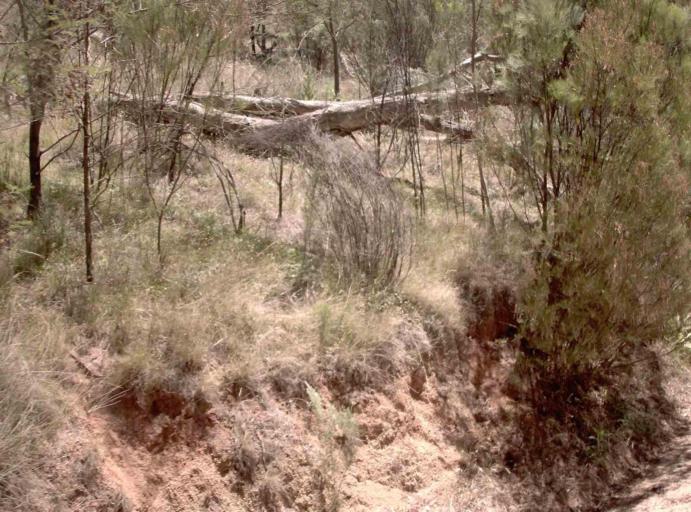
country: AU
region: New South Wales
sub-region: Snowy River
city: Jindabyne
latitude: -36.9171
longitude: 148.4212
